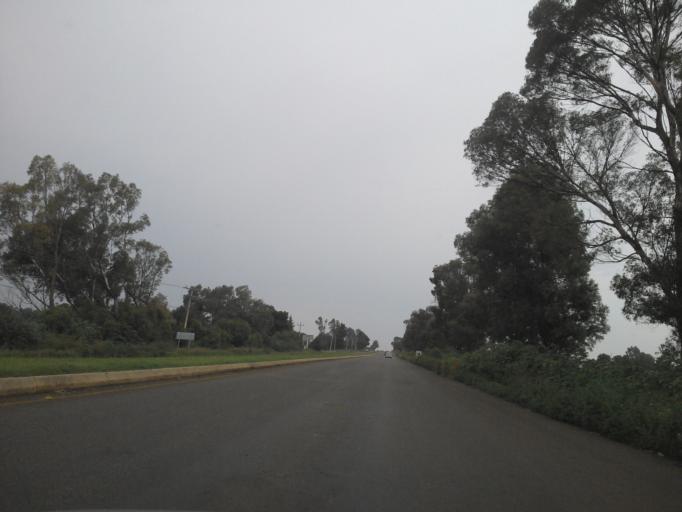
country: MX
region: Jalisco
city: Capilla de Guadalupe
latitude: 20.7749
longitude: -102.5542
